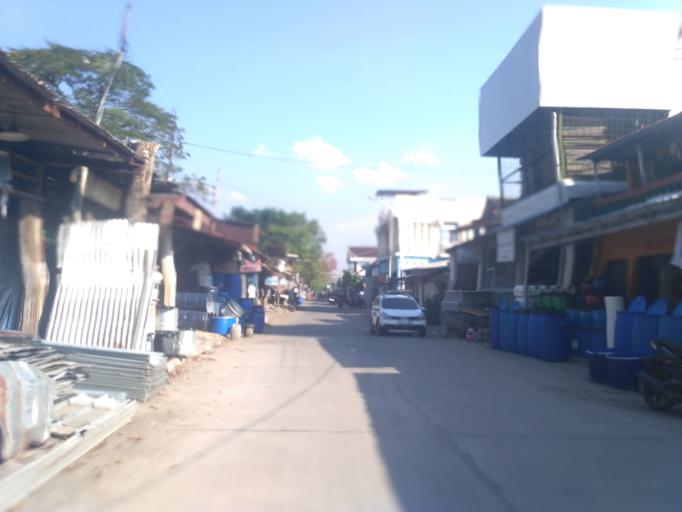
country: ID
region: Central Java
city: Semarang
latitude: -6.9732
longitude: 110.4421
